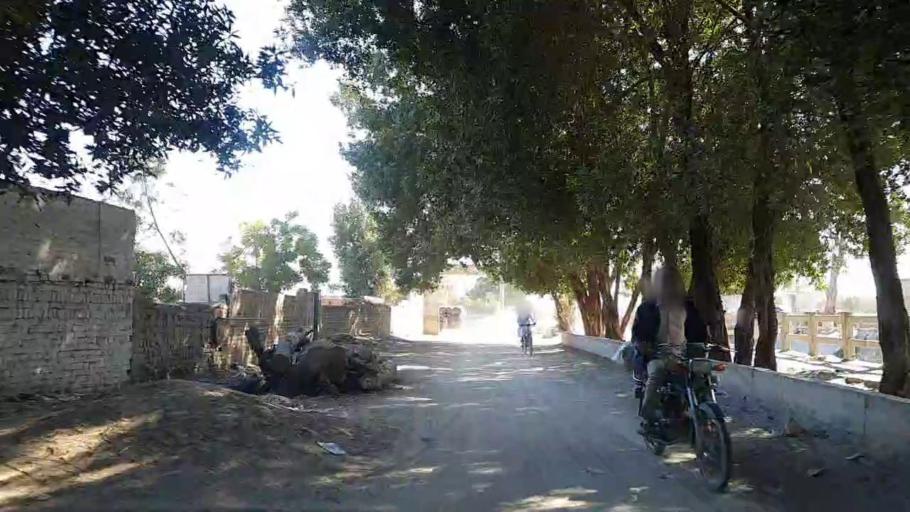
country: PK
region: Sindh
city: Nawabshah
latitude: 26.2448
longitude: 68.4221
